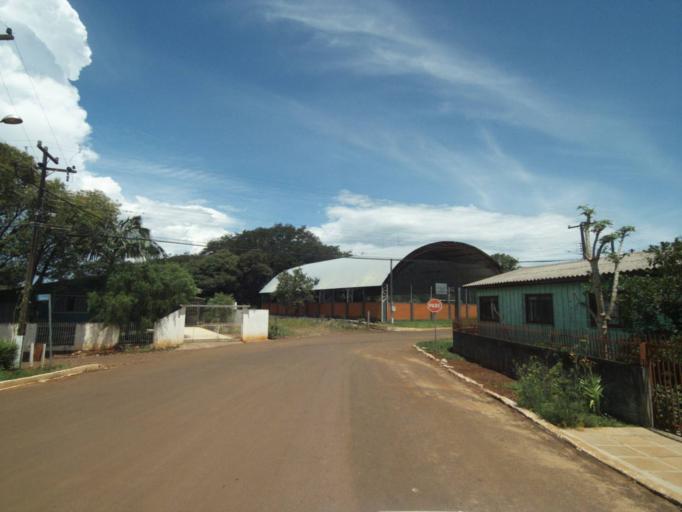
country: BR
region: Parana
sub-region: Guaraniacu
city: Guaraniacu
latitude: -25.0921
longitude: -52.8742
